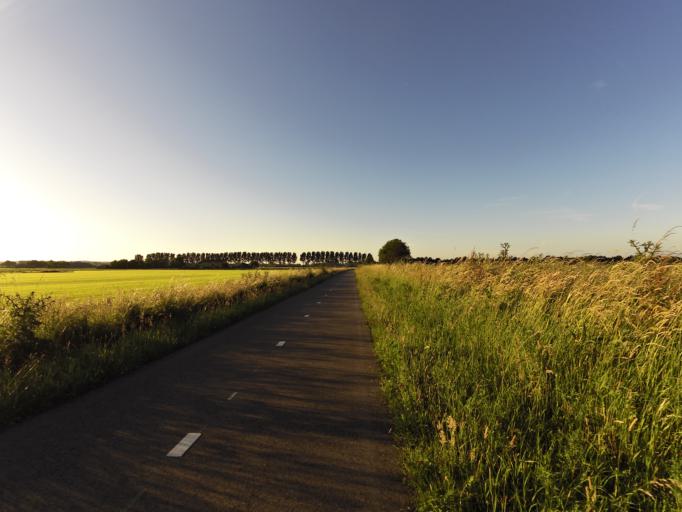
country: NL
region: Gelderland
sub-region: Gemeente Zevenaar
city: Zevenaar
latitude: 51.9766
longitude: 6.0898
